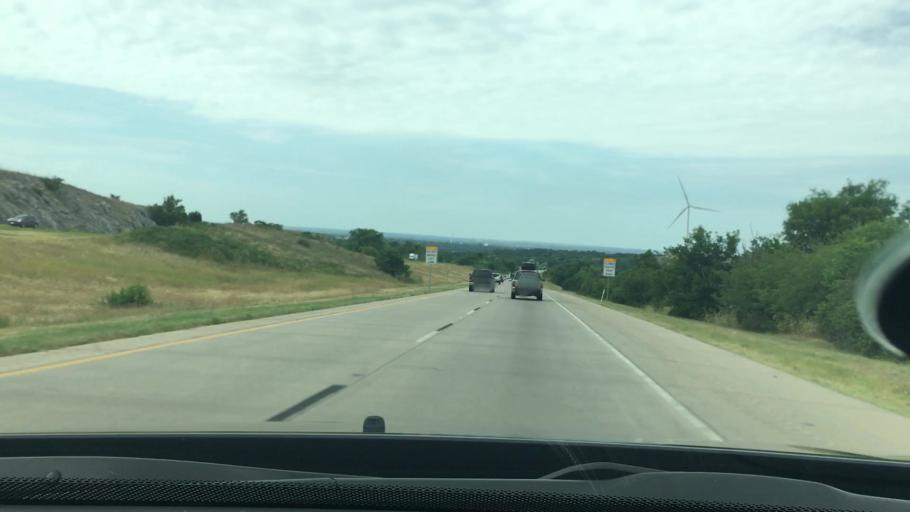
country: US
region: Oklahoma
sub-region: Murray County
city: Davis
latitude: 34.3711
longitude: -97.1463
